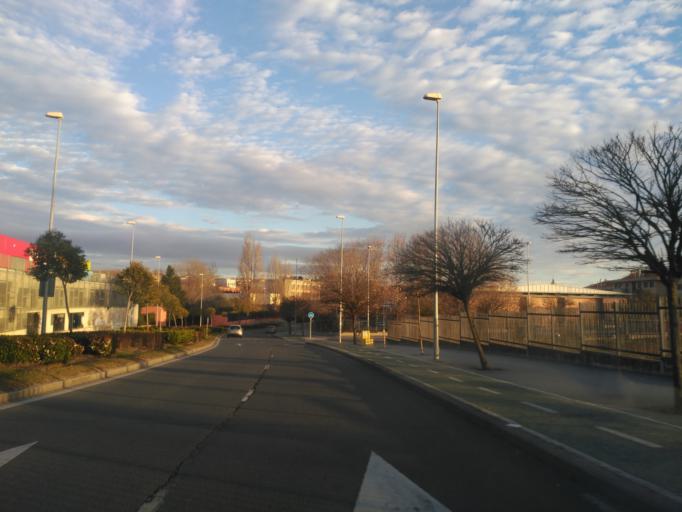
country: ES
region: Castille and Leon
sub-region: Provincia de Salamanca
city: Salamanca
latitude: 40.9718
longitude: -5.6805
